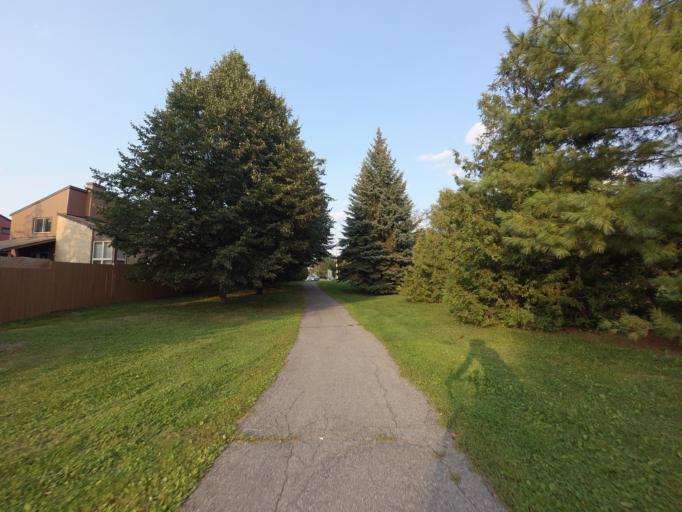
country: CA
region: Ontario
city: Bells Corners
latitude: 45.2816
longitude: -75.7602
